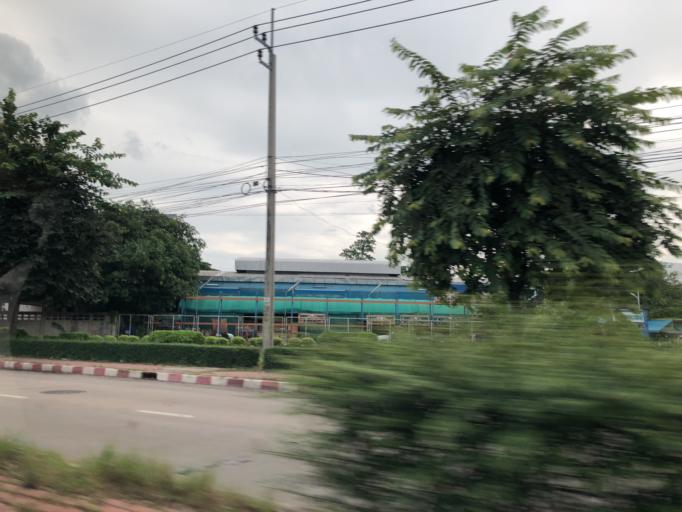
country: TH
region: Nonthaburi
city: Pak Kret
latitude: 13.9121
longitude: 100.5205
